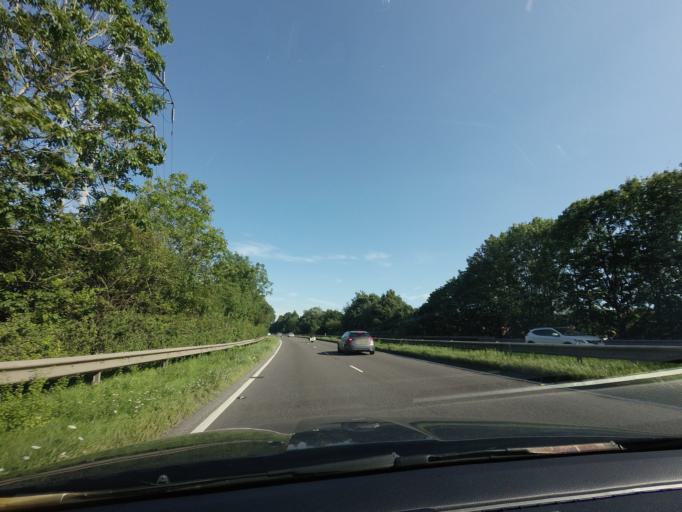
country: GB
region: England
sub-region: Derbyshire
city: Chesterfield
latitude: 53.2264
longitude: -1.4112
